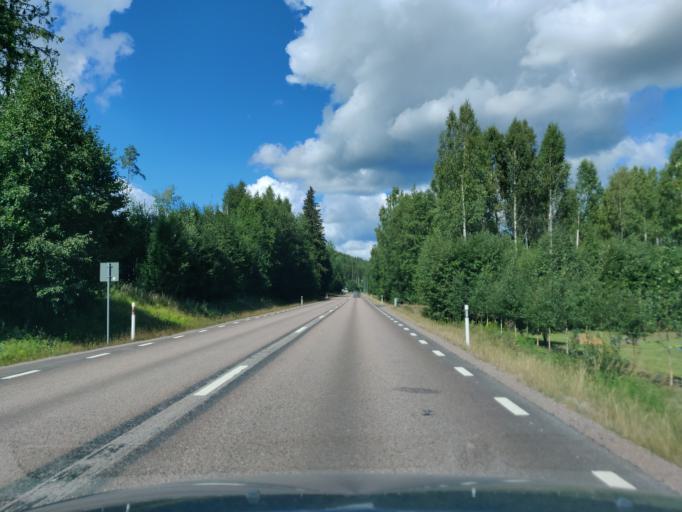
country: SE
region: Vaermland
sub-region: Hagfors Kommun
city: Ekshaerad
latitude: 60.0912
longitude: 13.5513
